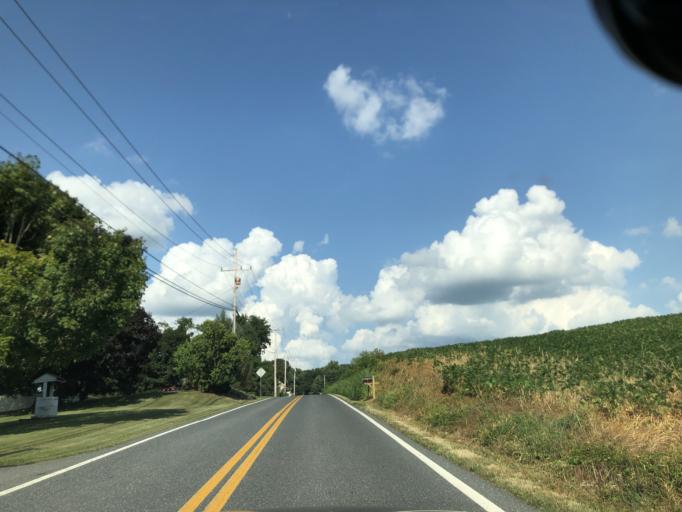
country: US
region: Maryland
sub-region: Frederick County
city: Linganore
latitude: 39.4700
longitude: -77.1655
